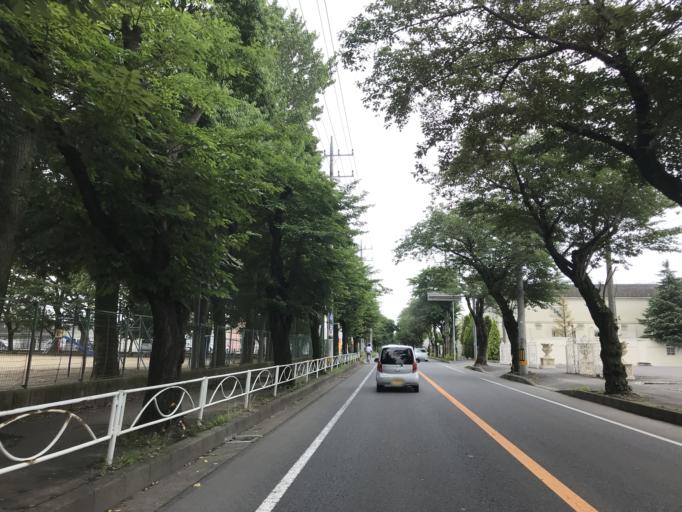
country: JP
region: Ibaraki
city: Mito-shi
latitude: 36.3344
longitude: 140.4608
